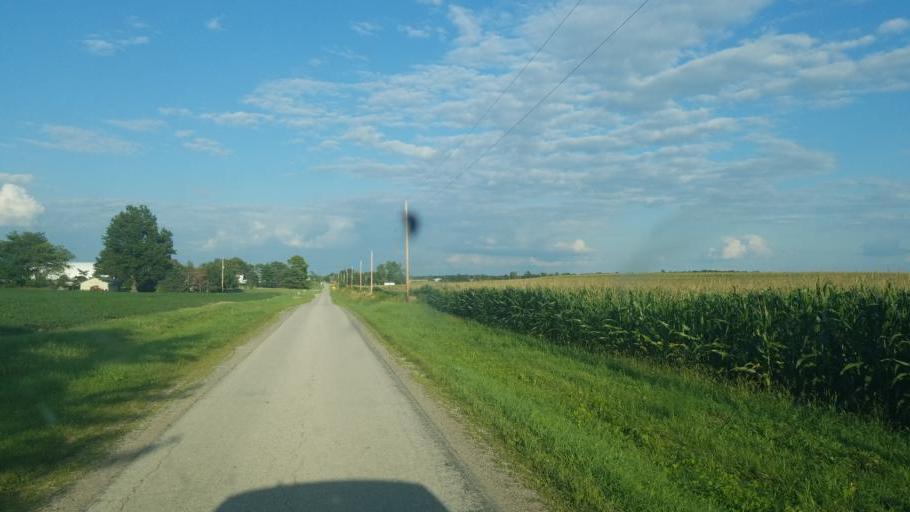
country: US
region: Ohio
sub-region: Sandusky County
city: Mount Carmel
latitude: 41.1100
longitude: -82.8976
